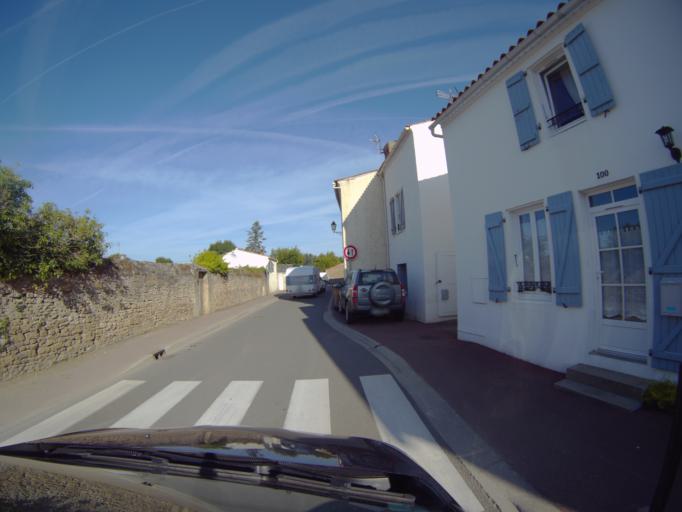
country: FR
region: Pays de la Loire
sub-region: Departement de la Vendee
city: Saint-Hilaire-de-Talmont
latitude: 46.4708
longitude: -1.6042
